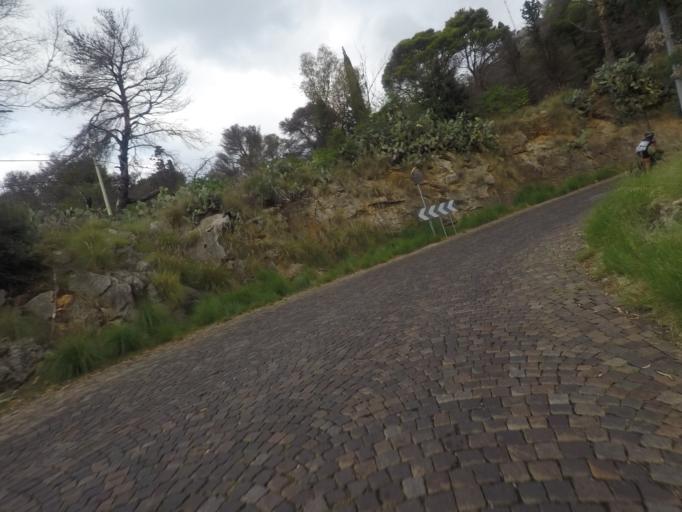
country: IT
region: Sicily
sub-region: Palermo
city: Palermo
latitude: 38.1546
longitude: 13.3591
